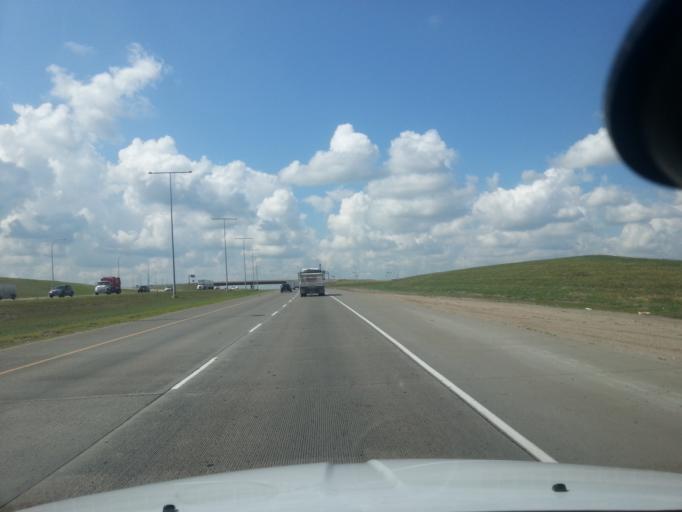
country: CA
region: Alberta
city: Devon
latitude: 53.4642
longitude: -113.6235
